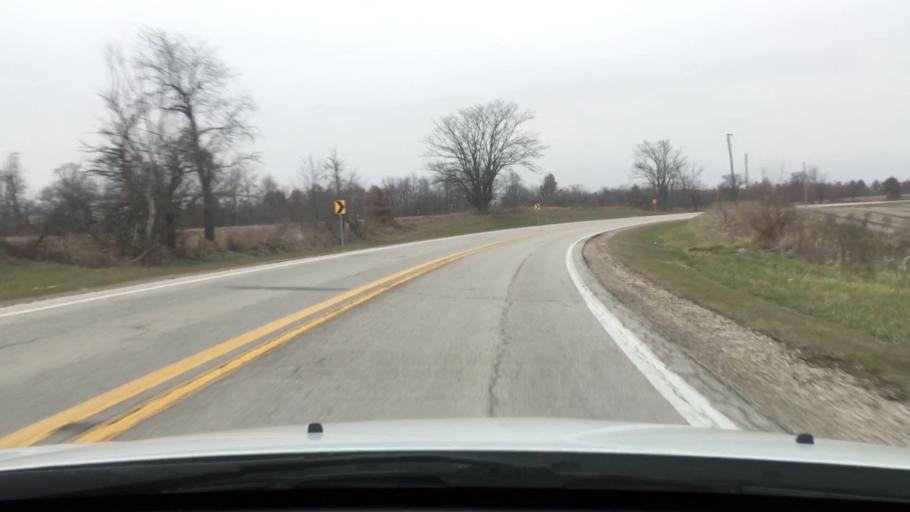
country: US
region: Illinois
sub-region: Pike County
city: Pittsfield
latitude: 39.5914
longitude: -90.8975
